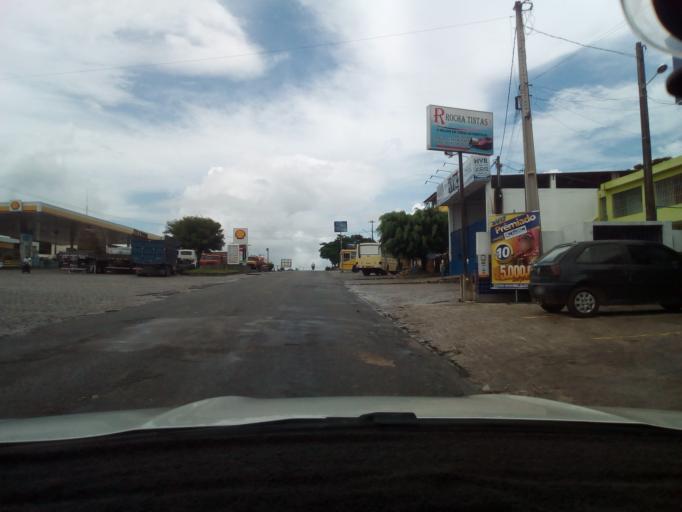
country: BR
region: Paraiba
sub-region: Pedras De Fogo
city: Pedras de Fogo
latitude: -7.4039
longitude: -35.1235
